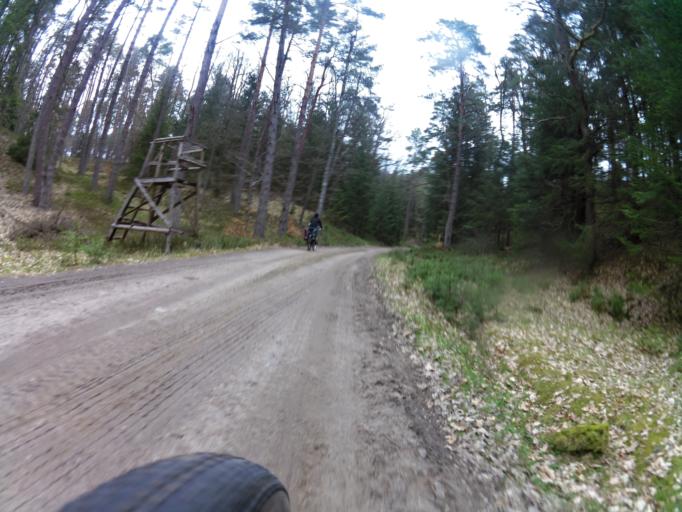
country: PL
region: West Pomeranian Voivodeship
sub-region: Powiat koszalinski
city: Polanow
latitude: 54.1779
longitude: 16.6593
